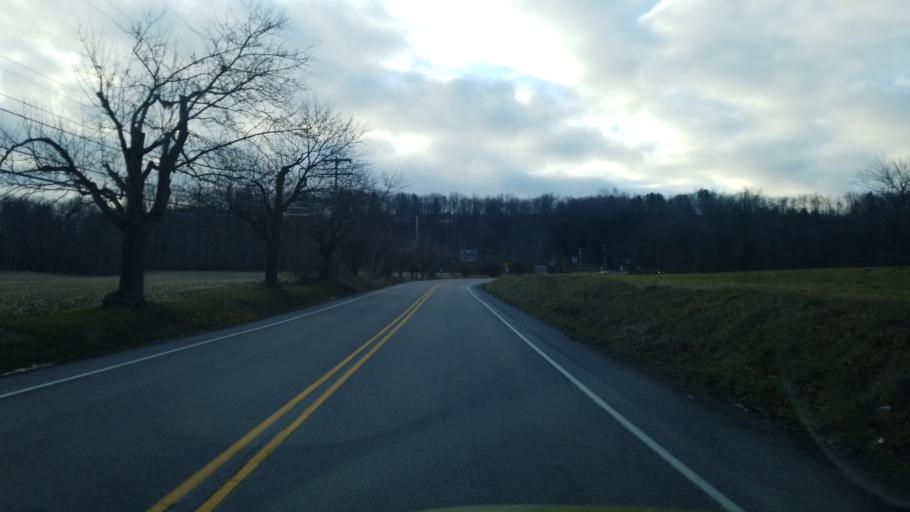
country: US
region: Pennsylvania
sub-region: Clearfield County
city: Clearfield
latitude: 41.0059
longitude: -78.4274
